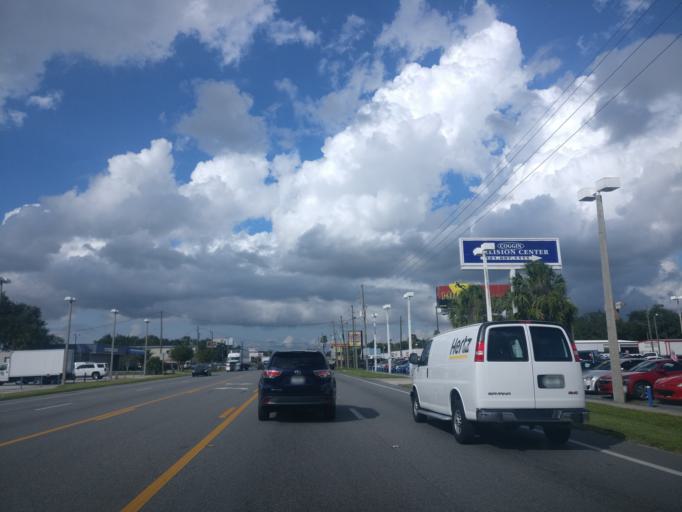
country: US
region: Florida
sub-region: Osceola County
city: Kissimmee
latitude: 28.3200
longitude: -81.4037
